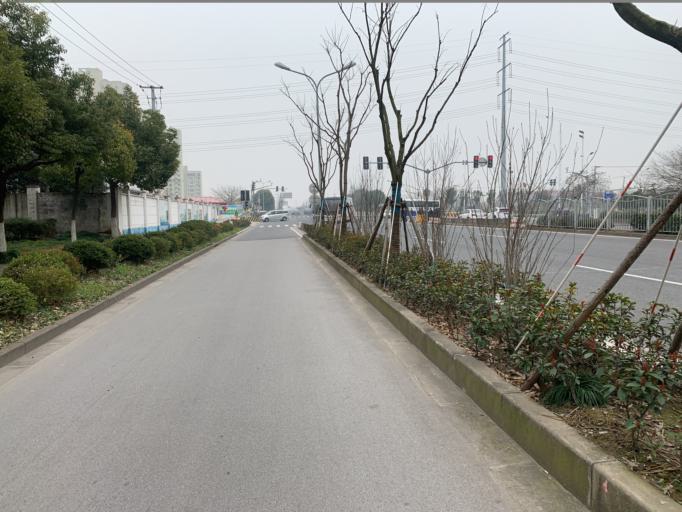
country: CN
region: Shanghai Shi
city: Huamu
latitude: 31.2451
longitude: 121.6212
